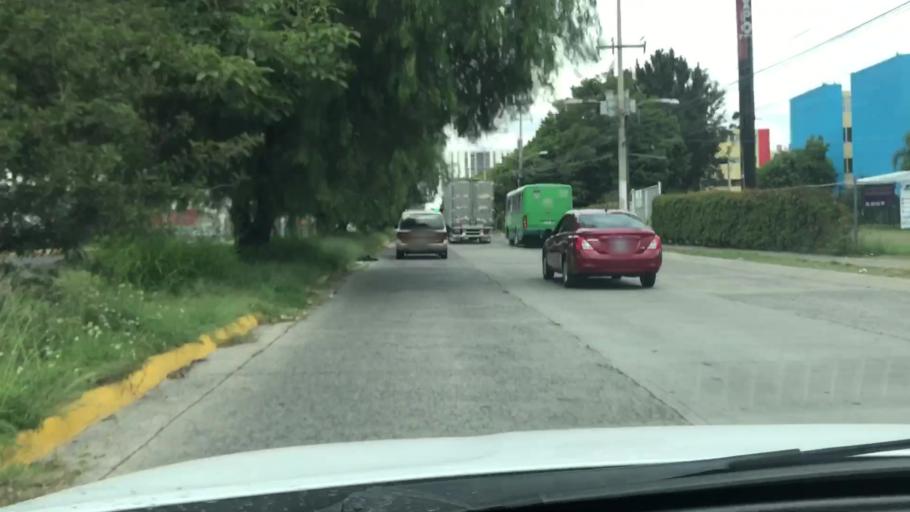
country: MX
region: Jalisco
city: Guadalajara
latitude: 20.6522
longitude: -103.4324
